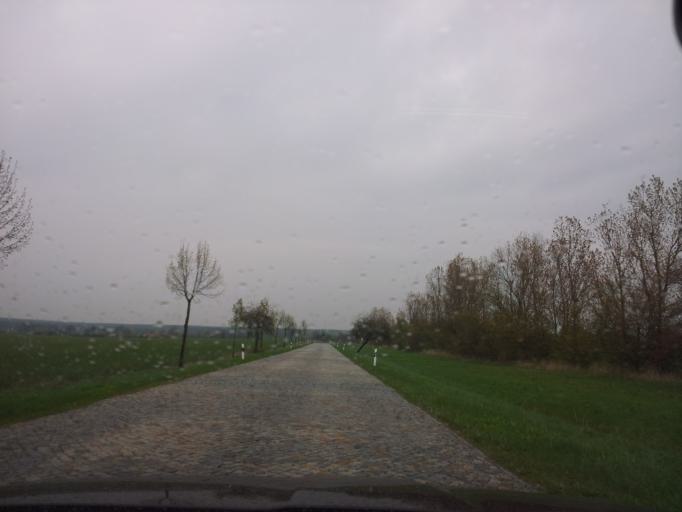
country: DE
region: Brandenburg
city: Niedergorsdorf
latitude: 52.0061
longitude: 12.9171
